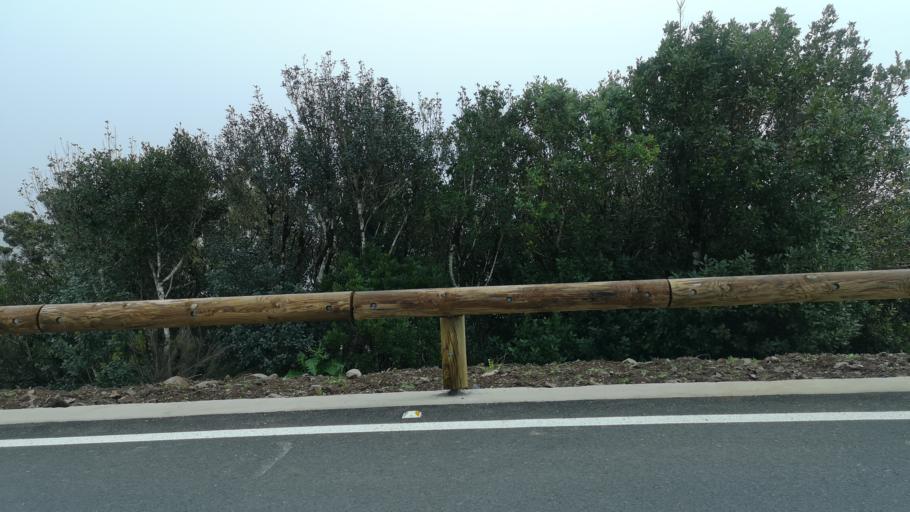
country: ES
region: Canary Islands
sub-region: Provincia de Santa Cruz de Tenerife
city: Vallehermosa
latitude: 28.1493
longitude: -17.3083
